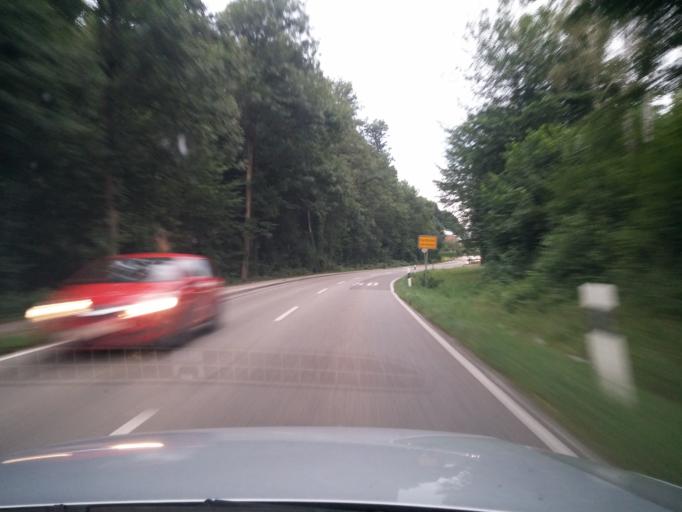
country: DE
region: Baden-Wuerttemberg
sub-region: Tuebingen Region
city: Aitrach
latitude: 47.9438
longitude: 10.1092
